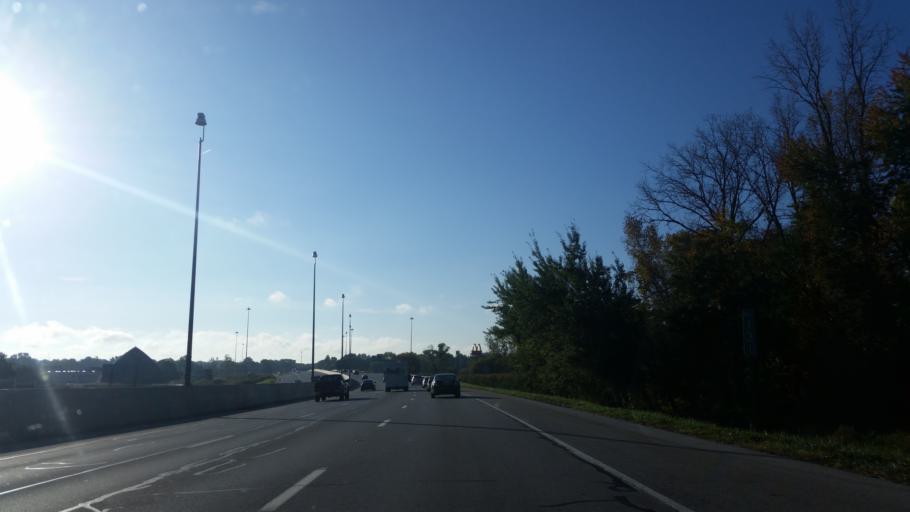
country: US
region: Ohio
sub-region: Summit County
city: Fairlawn
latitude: 41.0882
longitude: -81.5832
